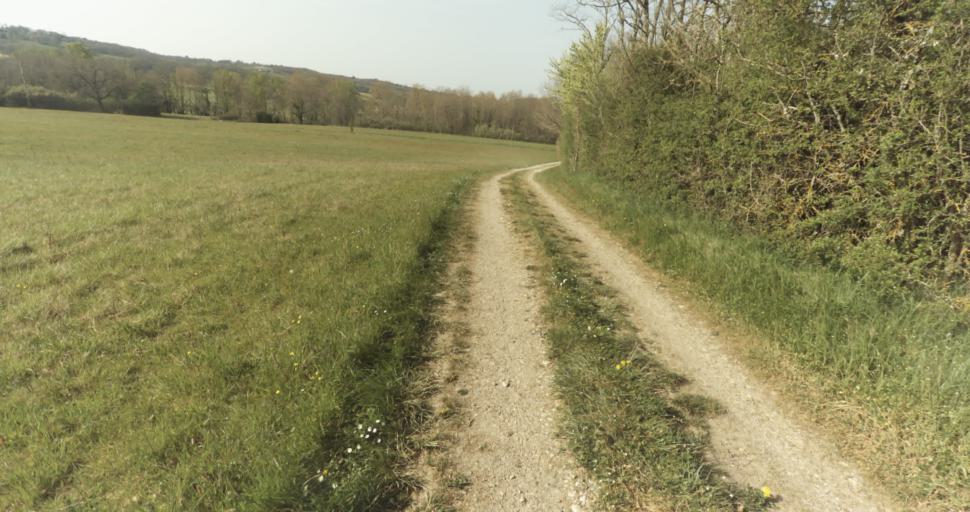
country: FR
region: Midi-Pyrenees
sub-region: Departement du Tarn-et-Garonne
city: Lafrancaise
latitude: 44.1255
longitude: 1.1669
